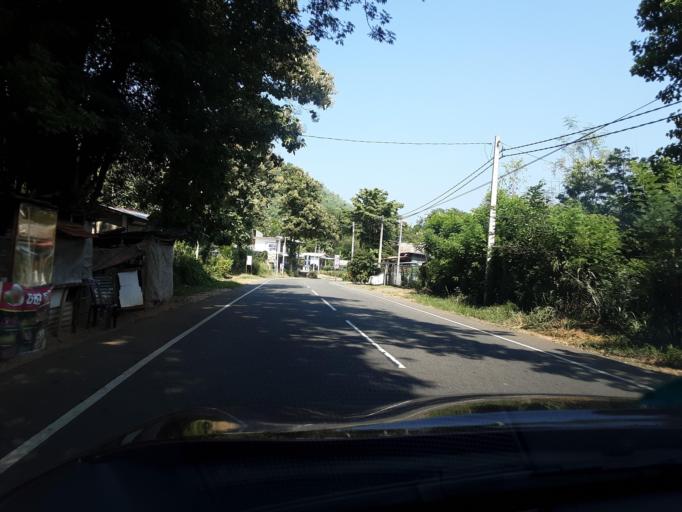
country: LK
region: Uva
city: Badulla
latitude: 7.1673
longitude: 81.0517
